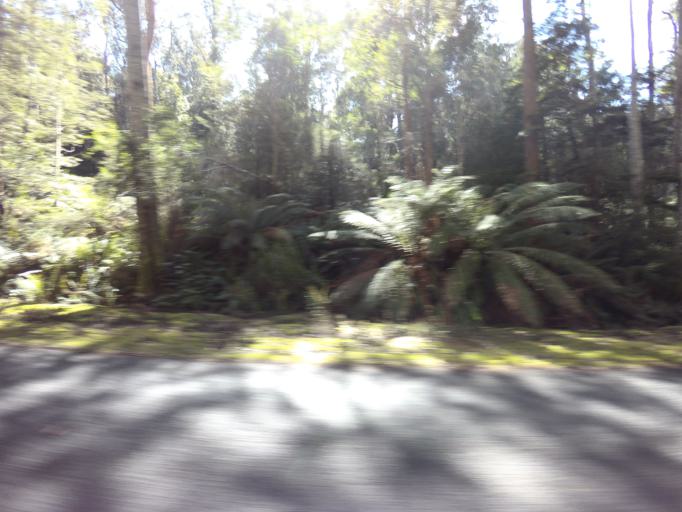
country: AU
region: Tasmania
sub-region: Derwent Valley
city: New Norfolk
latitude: -42.7527
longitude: 146.5234
